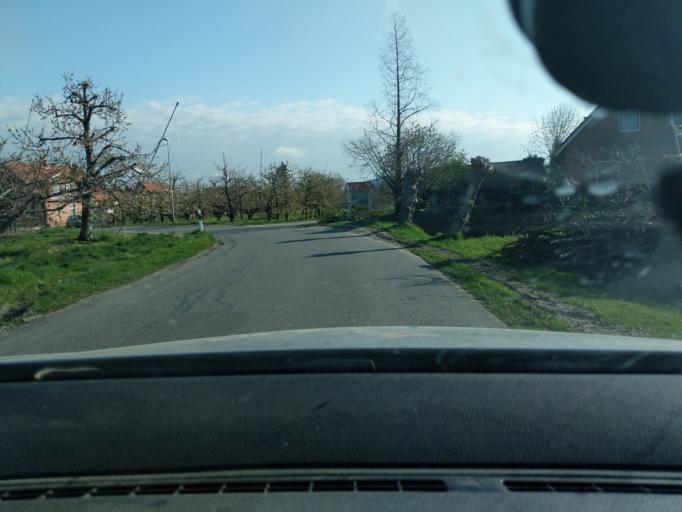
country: DE
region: Lower Saxony
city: Grunendeich
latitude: 53.5669
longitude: 9.6398
